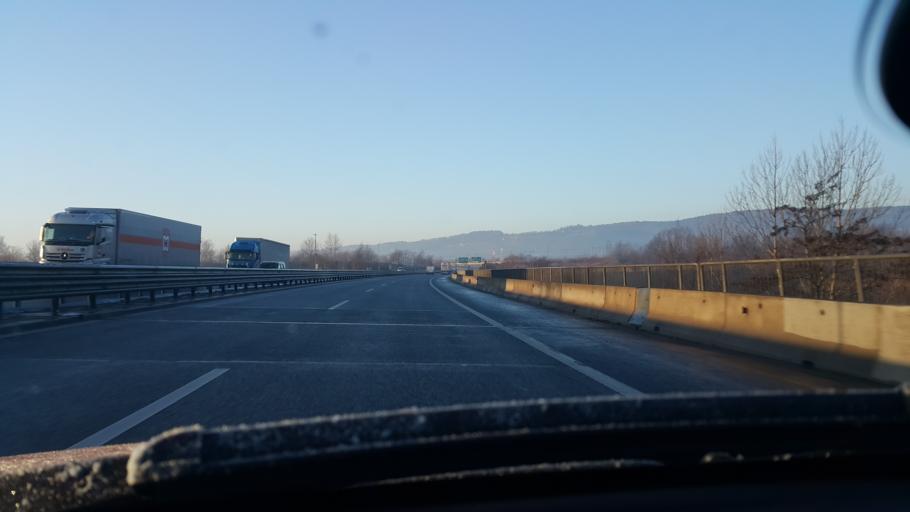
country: SI
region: Hoce-Slivnica
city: Rogoza
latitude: 46.4921
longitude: 15.6680
